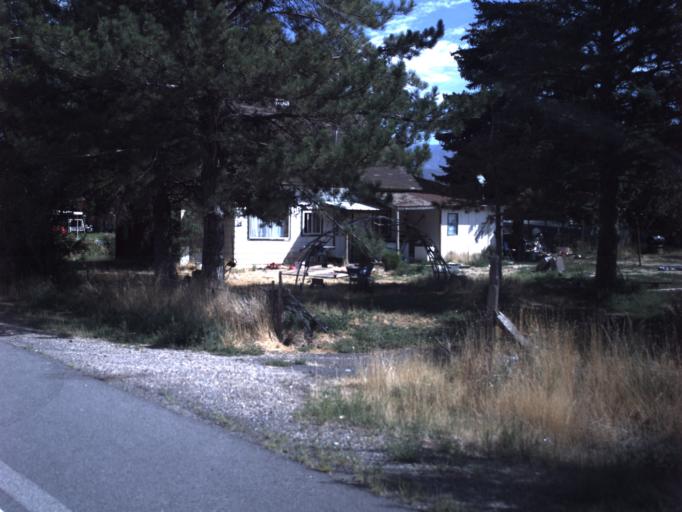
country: US
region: Utah
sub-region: Juab County
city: Nephi
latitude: 39.5525
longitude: -111.8638
